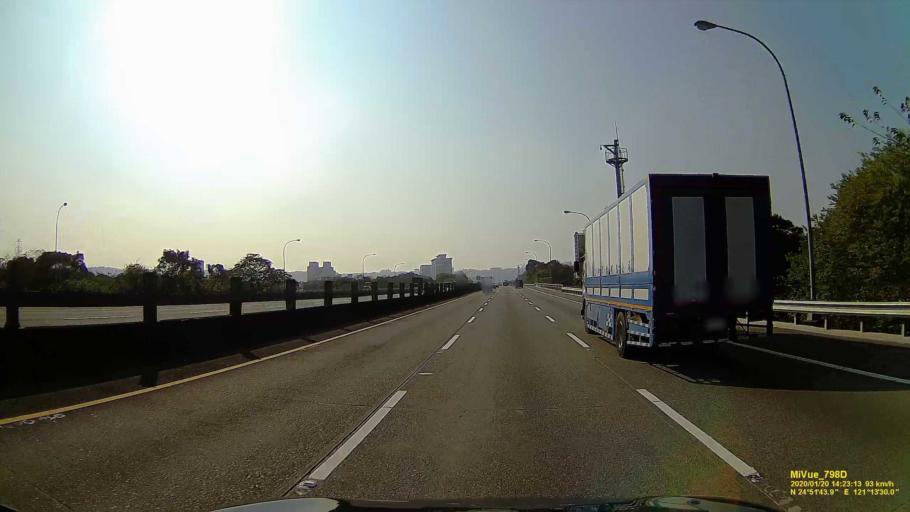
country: TW
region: Taiwan
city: Daxi
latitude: 24.8629
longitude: 121.2261
